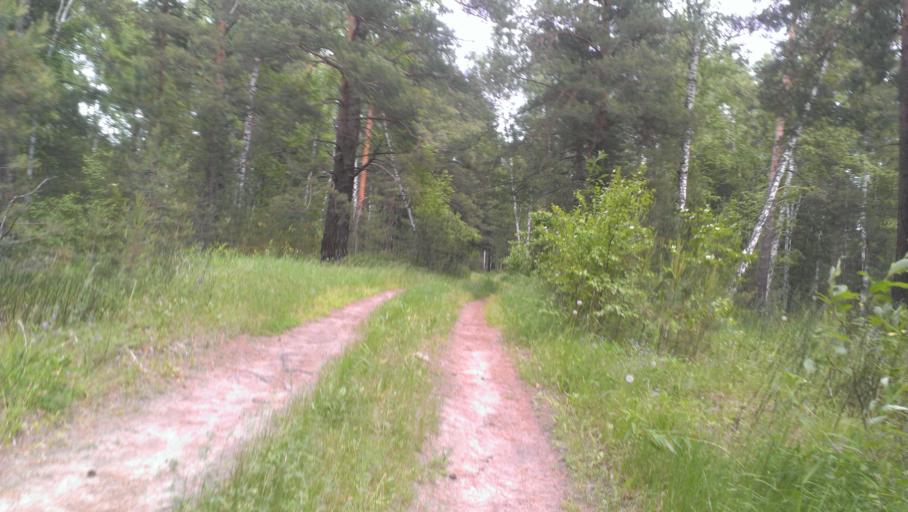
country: RU
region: Altai Krai
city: Sannikovo
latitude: 53.3492
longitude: 84.0347
